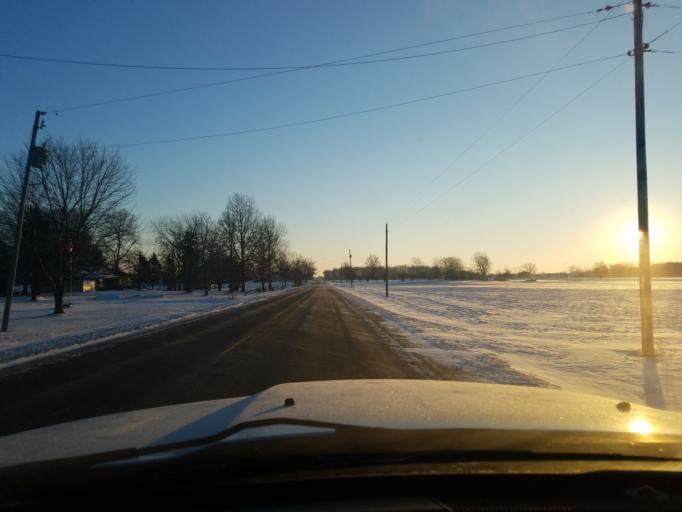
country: US
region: Indiana
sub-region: Marshall County
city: Plymouth
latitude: 41.4496
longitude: -86.2738
